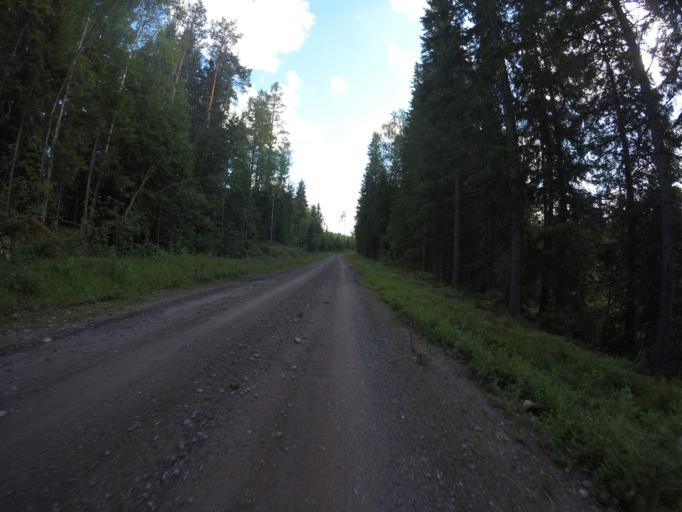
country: SE
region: OErebro
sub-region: Hallefors Kommun
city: Haellefors
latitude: 60.0060
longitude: 14.6090
